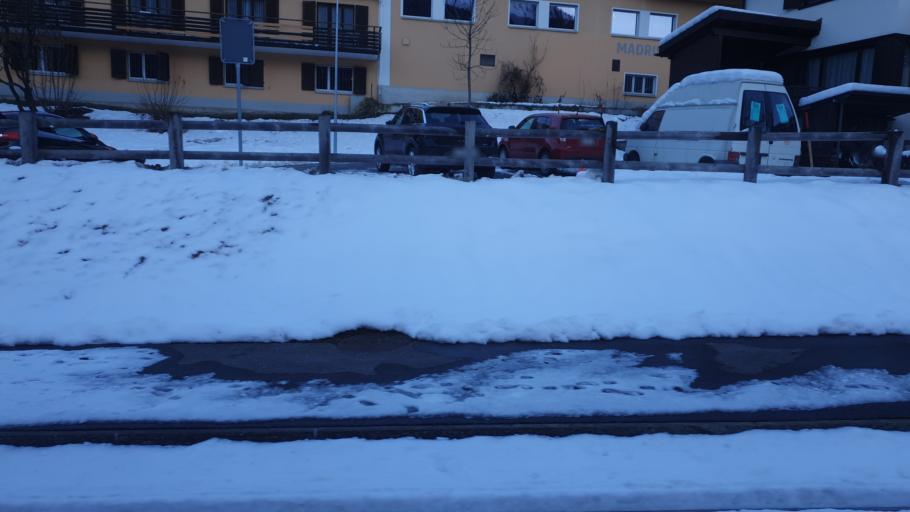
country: CH
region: Grisons
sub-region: Praettigau/Davos District
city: Klosters Serneus
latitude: 46.8829
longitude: 9.8759
